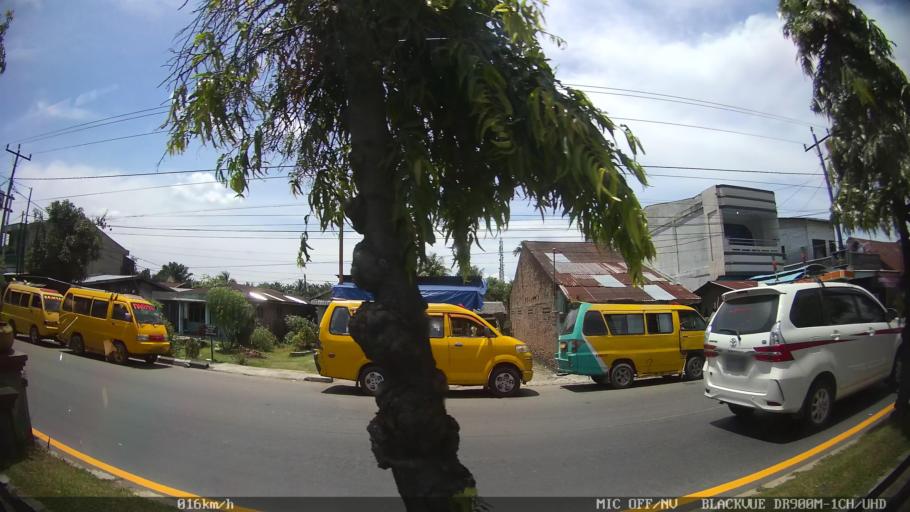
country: ID
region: North Sumatra
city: Binjai
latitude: 3.6086
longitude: 98.5022
